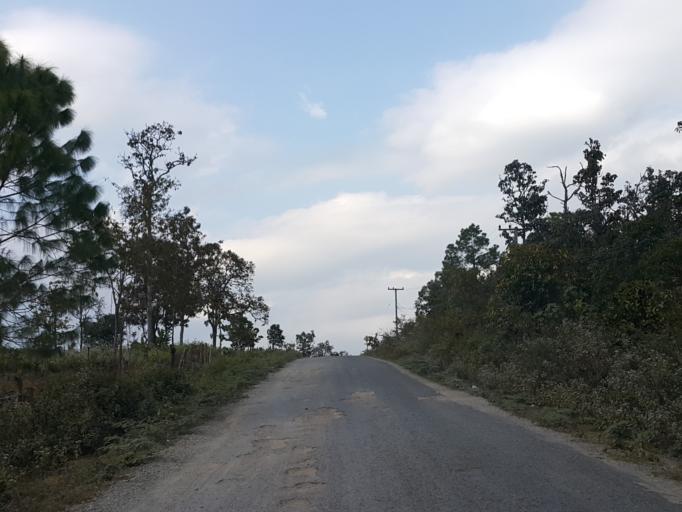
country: TH
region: Chiang Mai
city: Om Koi
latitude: 17.8108
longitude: 98.3305
